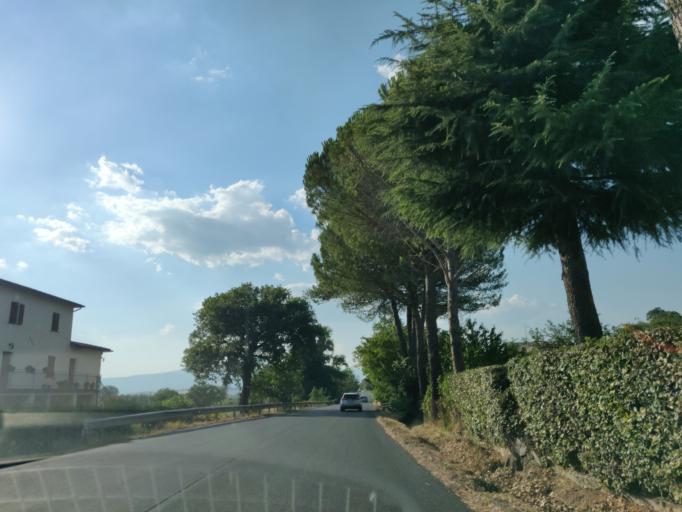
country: IT
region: Latium
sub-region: Provincia di Viterbo
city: Proceno
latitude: 42.7875
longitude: 11.8258
